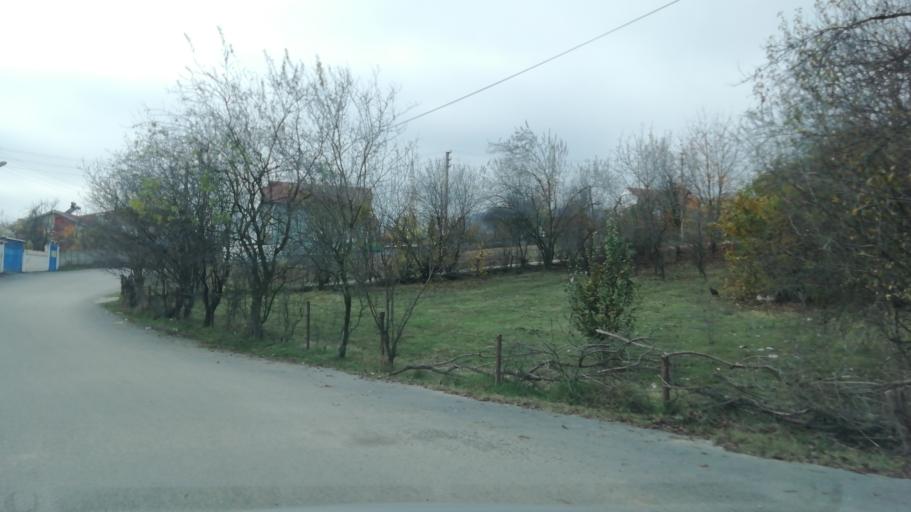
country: TR
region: Karabuk
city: Karabuk
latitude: 41.2316
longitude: 32.6271
